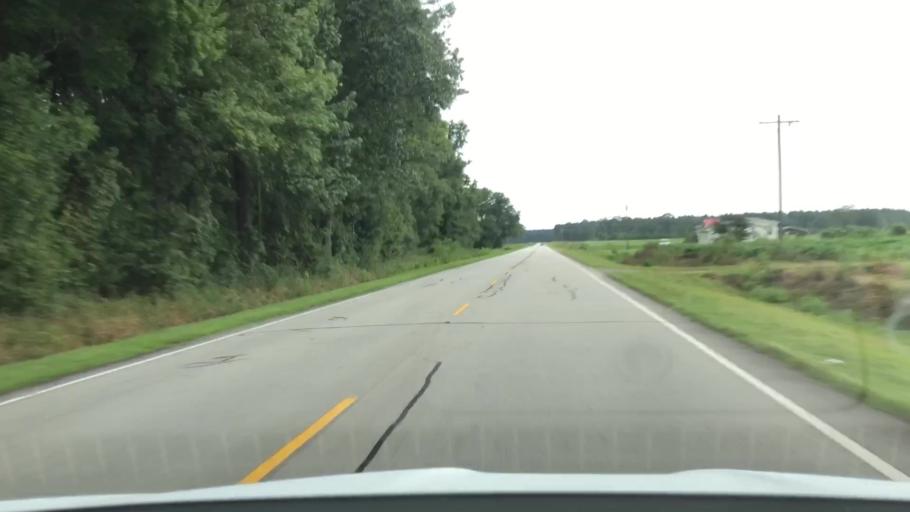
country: US
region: North Carolina
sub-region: Jones County
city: Trenton
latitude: 35.1035
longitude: -77.4945
